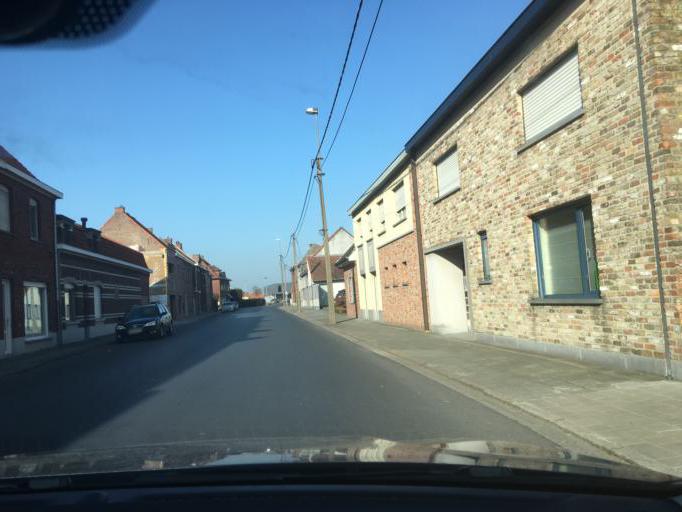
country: BE
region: Flanders
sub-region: Provincie West-Vlaanderen
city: Ledegem
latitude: 50.8595
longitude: 3.1338
